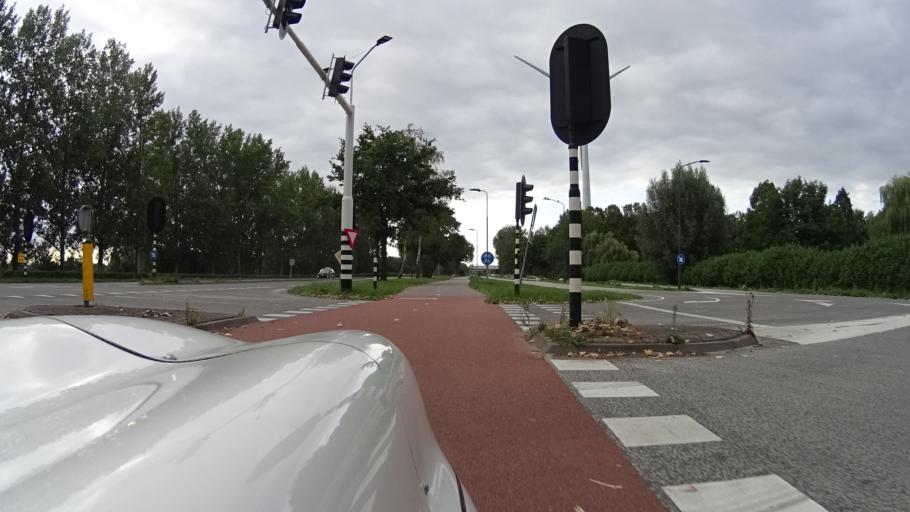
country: NL
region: North Brabant
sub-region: Gemeente 's-Hertogenbosch
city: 's-Hertogenbosch
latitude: 51.7148
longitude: 5.2901
